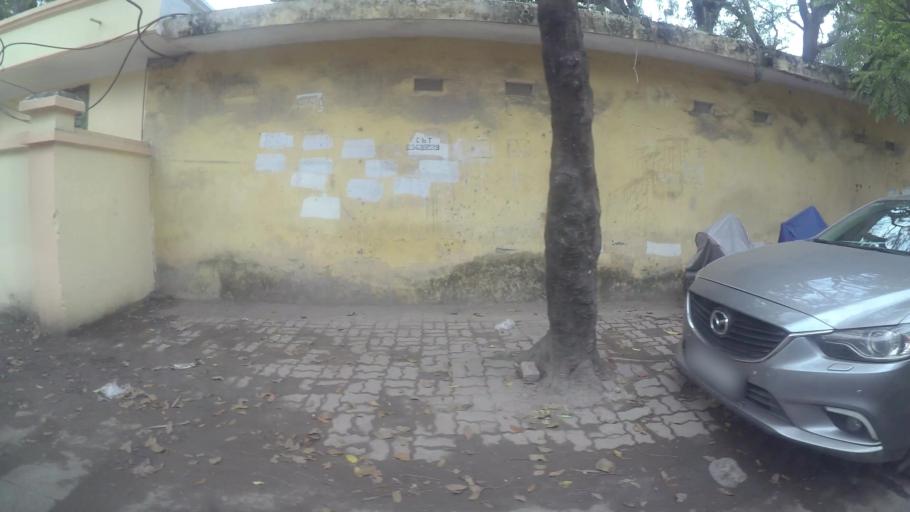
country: VN
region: Ha Noi
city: Tay Ho
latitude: 21.0714
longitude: 105.7964
